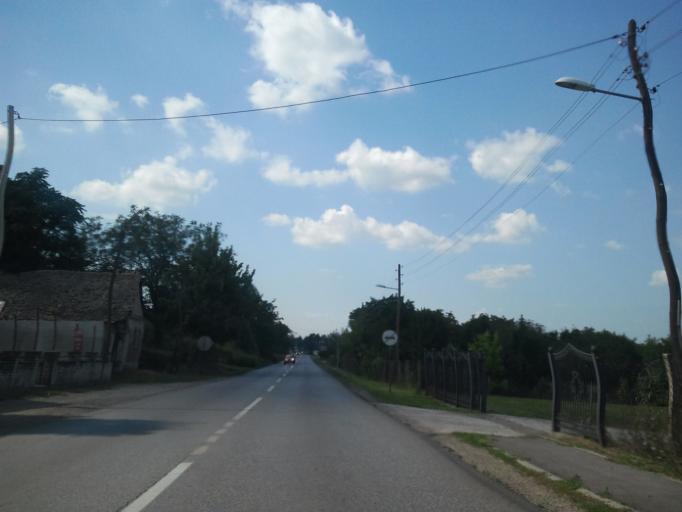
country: RS
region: Autonomna Pokrajina Vojvodina
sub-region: Juznobacki Okrug
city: Petrovaradin
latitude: 45.2288
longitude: 19.8958
